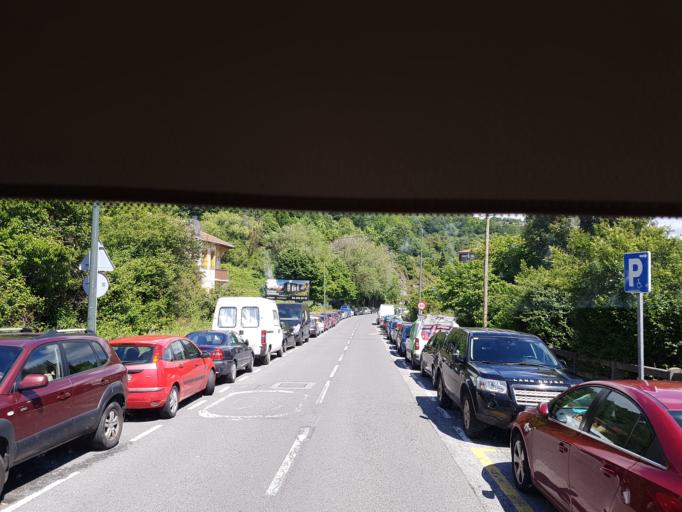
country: ES
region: Basque Country
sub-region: Bizkaia
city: Bilbao
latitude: 43.2693
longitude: -2.9187
